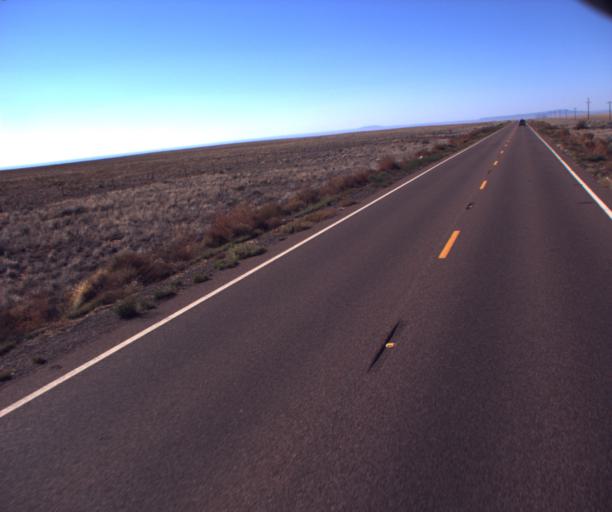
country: US
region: Arizona
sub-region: Navajo County
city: Winslow
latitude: 35.1107
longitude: -110.5216
